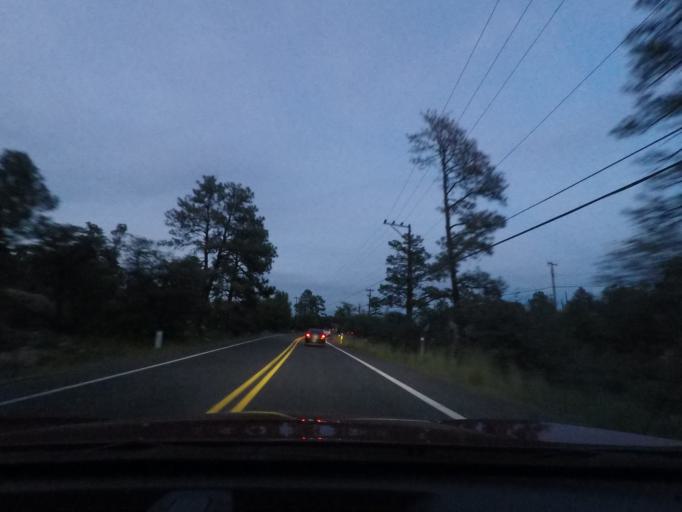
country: US
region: Arizona
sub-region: Yavapai County
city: Prescott
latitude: 34.5707
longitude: -112.5059
